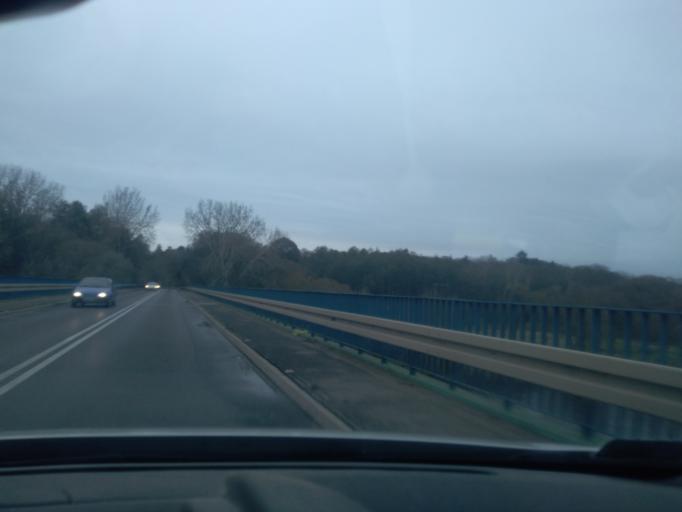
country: PL
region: Greater Poland Voivodeship
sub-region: Powiat poznanski
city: Murowana Goslina
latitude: 52.5410
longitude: 16.9588
